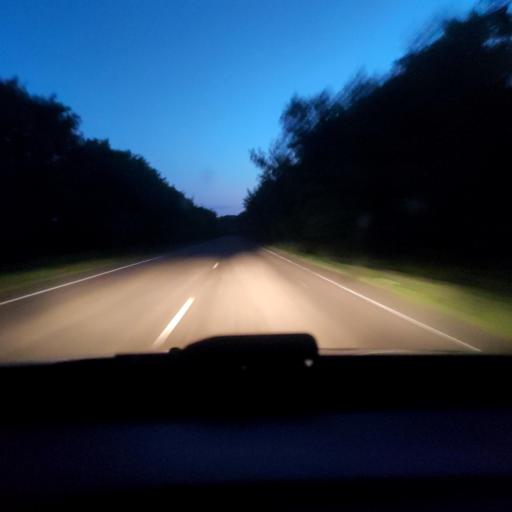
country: RU
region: Voronezj
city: Panino
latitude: 51.6326
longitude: 40.0722
